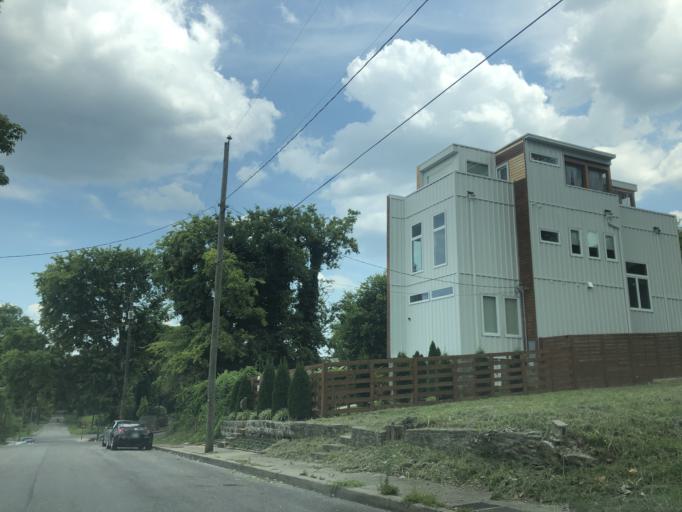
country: US
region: Tennessee
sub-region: Davidson County
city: Nashville
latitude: 36.1451
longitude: -86.7605
